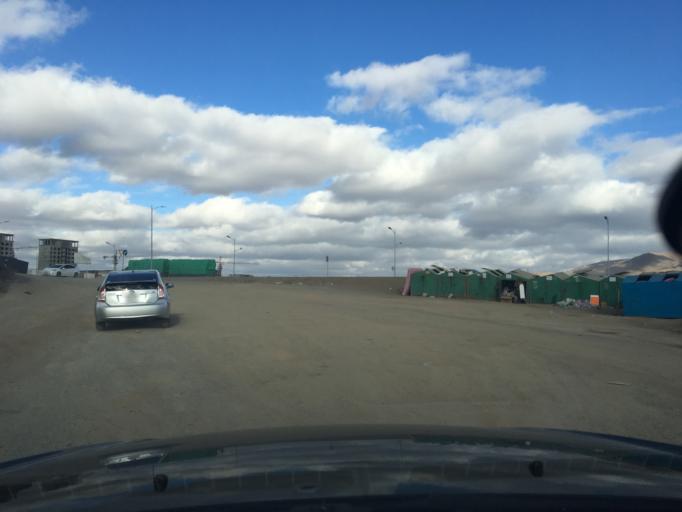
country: MN
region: Ulaanbaatar
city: Ulaanbaatar
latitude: 47.8453
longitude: 106.7897
